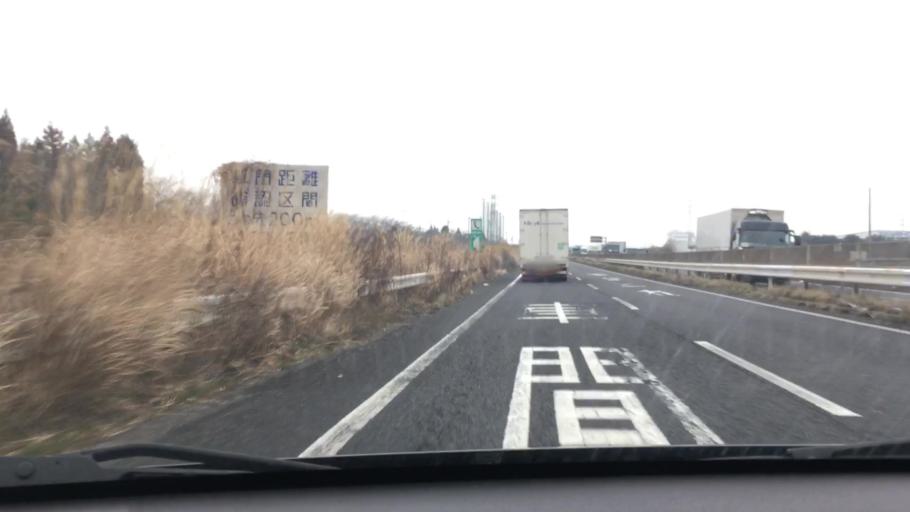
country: JP
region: Mie
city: Ueno-ebisumachi
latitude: 34.7159
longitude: 136.0805
